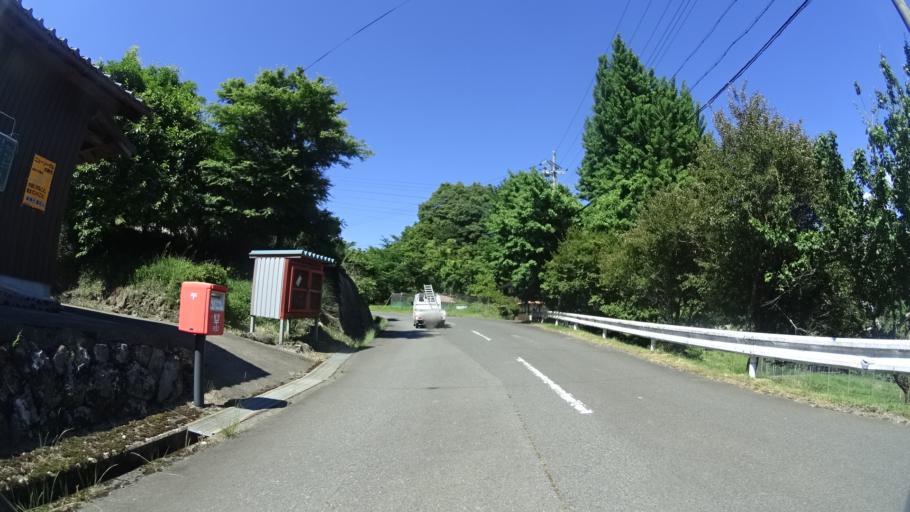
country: JP
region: Kyoto
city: Fukuchiyama
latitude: 35.3830
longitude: 135.0652
